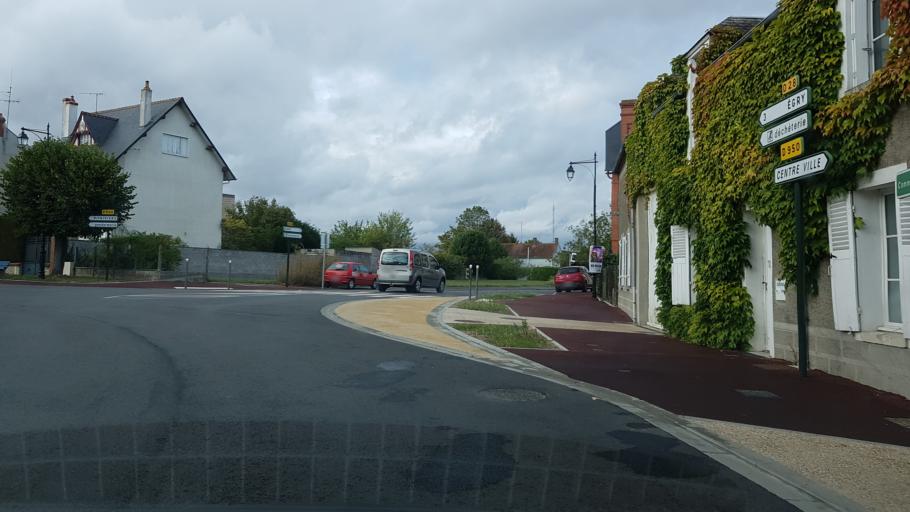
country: FR
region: Centre
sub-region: Departement du Loiret
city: Beaune-la-Rolande
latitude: 48.0718
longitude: 2.4293
